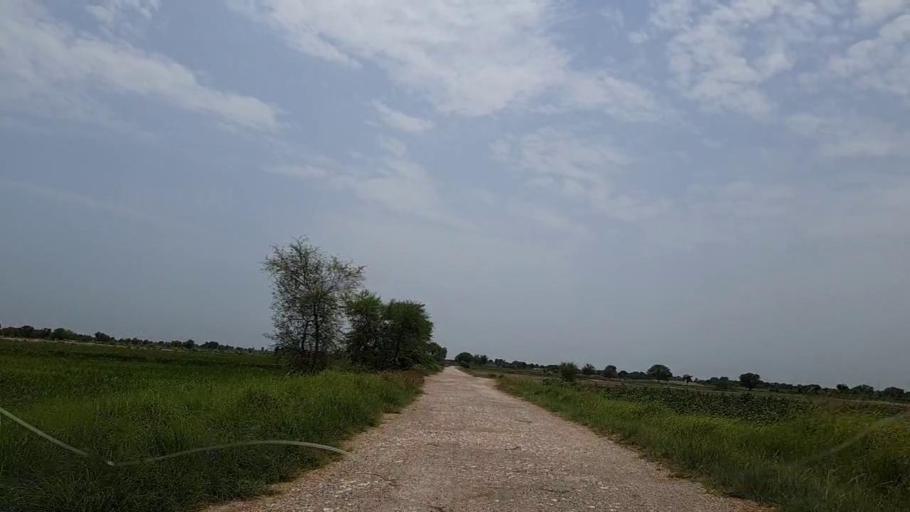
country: PK
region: Sindh
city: Tharu Shah
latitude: 26.9125
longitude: 68.0796
